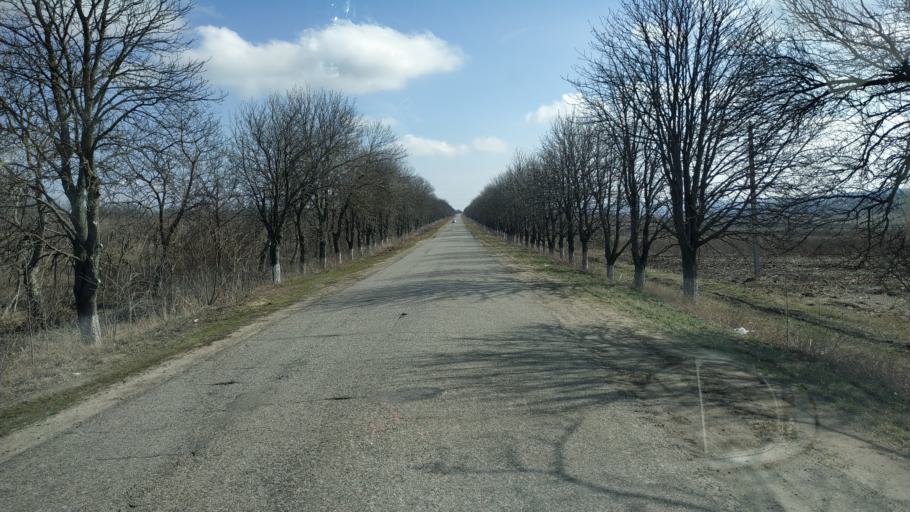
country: MD
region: Hincesti
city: Hincesti
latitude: 46.8567
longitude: 28.6372
